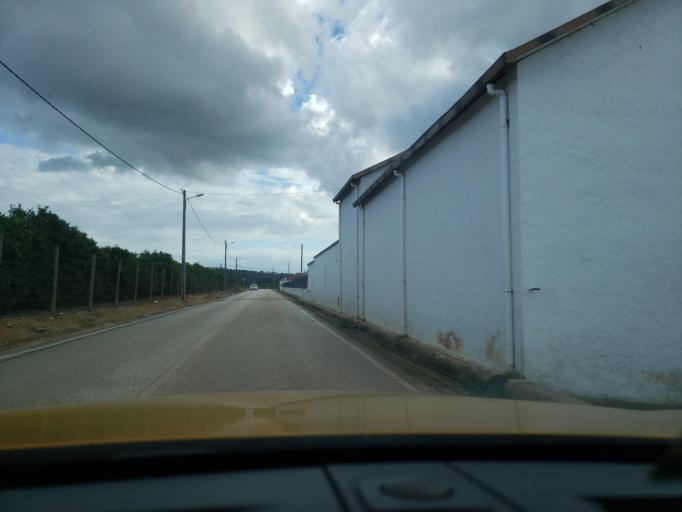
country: PT
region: Faro
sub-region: Portimao
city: Alvor
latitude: 37.1683
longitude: -8.5790
